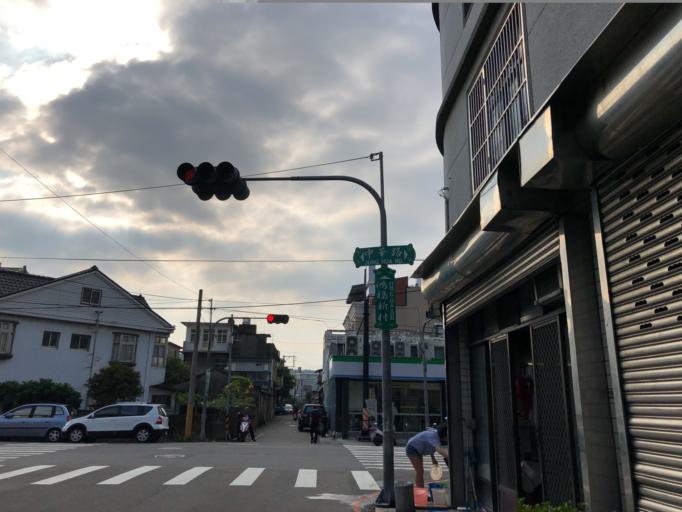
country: TW
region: Taiwan
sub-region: Miaoli
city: Miaoli
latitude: 24.5866
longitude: 120.8253
